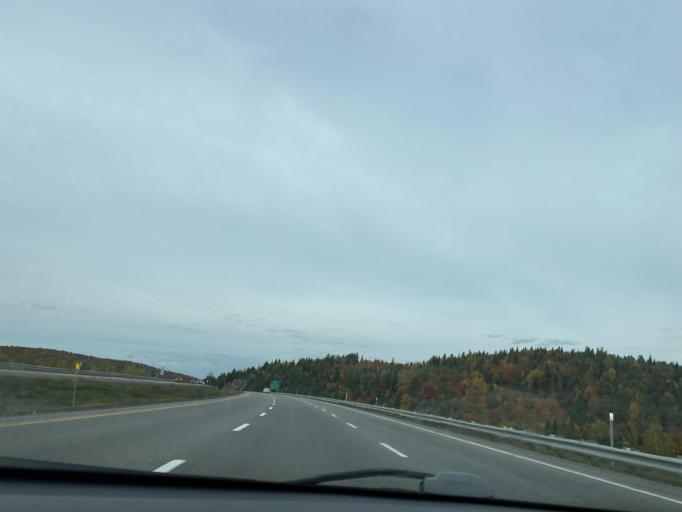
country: CA
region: Quebec
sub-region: Laurentides
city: Val-David
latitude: 45.9875
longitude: -74.1864
